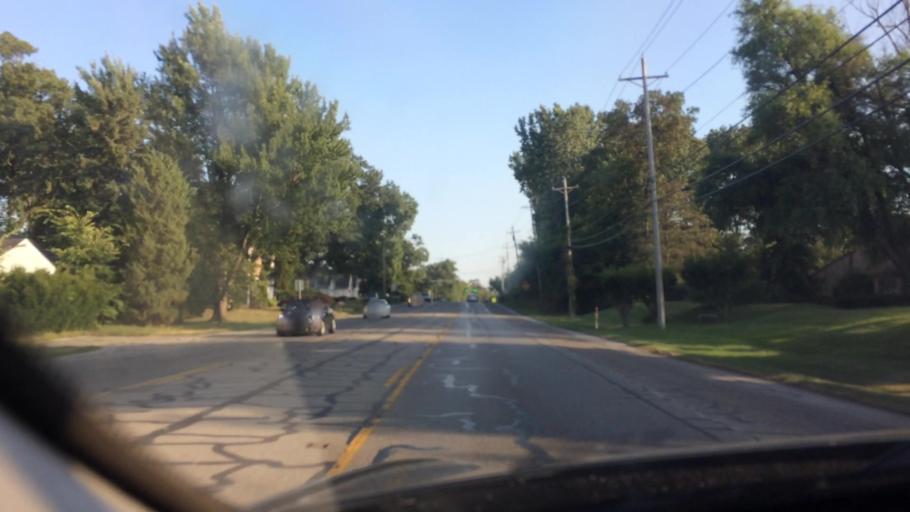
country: US
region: Ohio
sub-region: Lucas County
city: Holland
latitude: 41.6628
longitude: -83.7024
